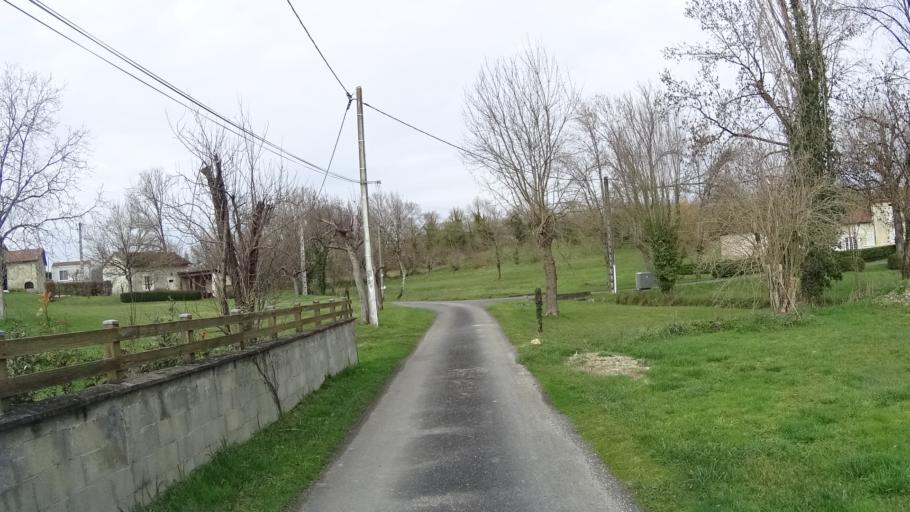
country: FR
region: Aquitaine
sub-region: Departement de la Dordogne
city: Saint-Aulaye
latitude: 45.2483
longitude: 0.1518
